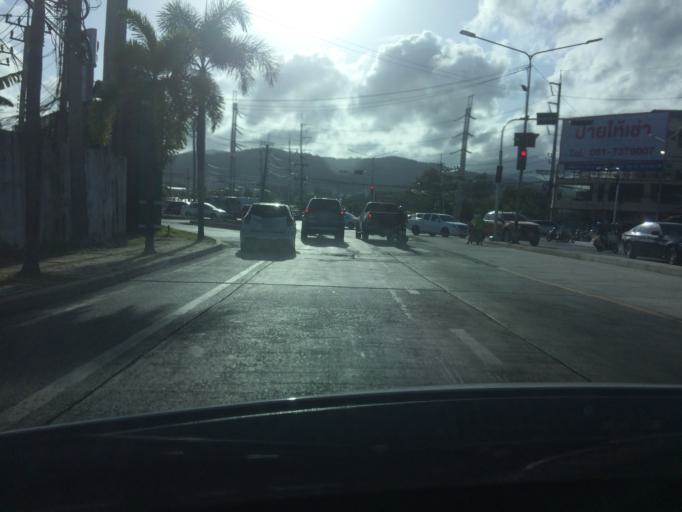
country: TH
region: Phuket
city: Mueang Phuket
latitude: 7.8696
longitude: 98.3754
